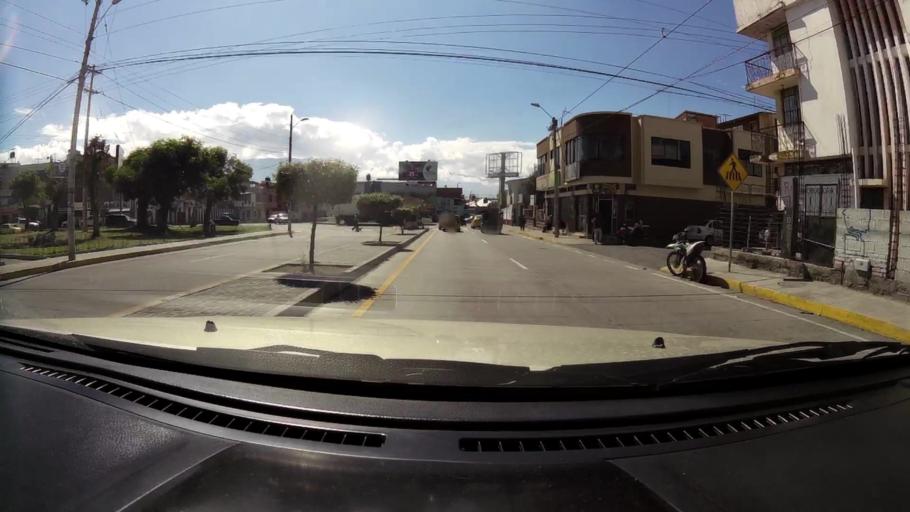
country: EC
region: Chimborazo
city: Riobamba
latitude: -1.6633
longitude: -78.6499
